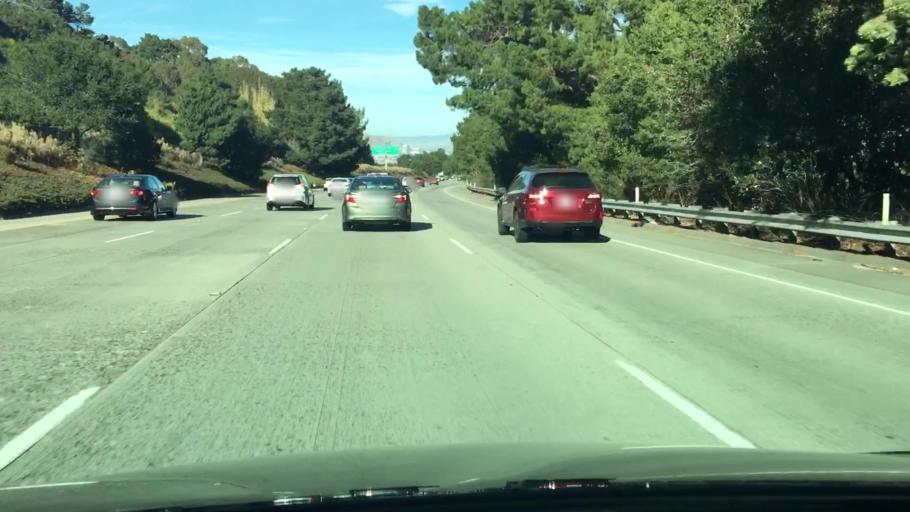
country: US
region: California
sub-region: San Mateo County
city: San Bruno
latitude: 37.6102
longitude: -122.4267
